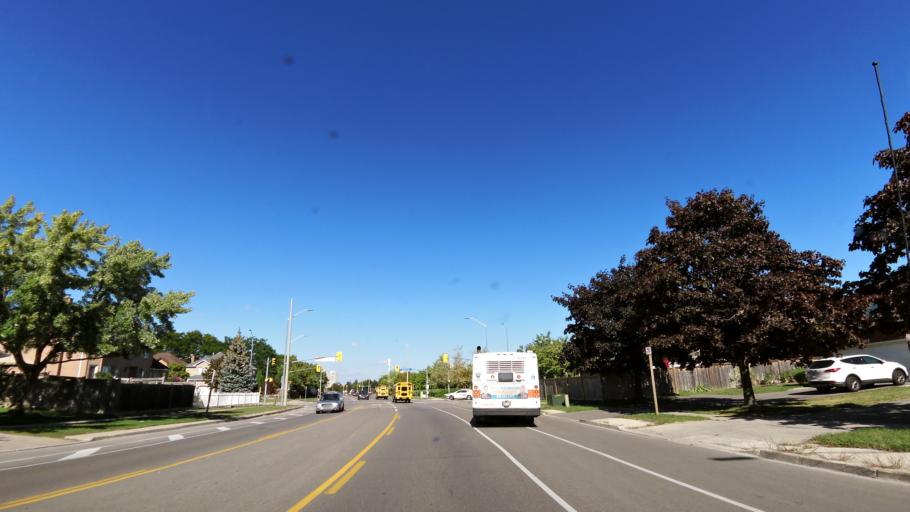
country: CA
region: Ontario
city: Mississauga
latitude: 43.6010
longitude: -79.6737
